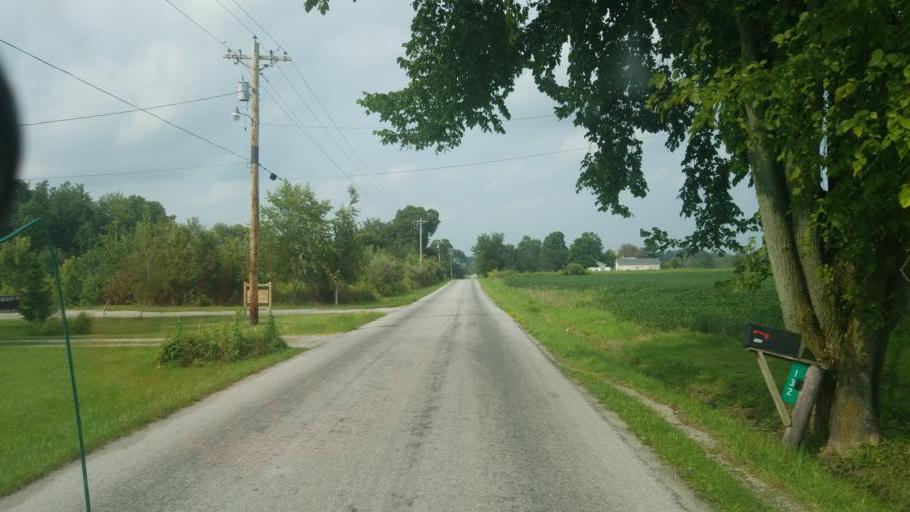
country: US
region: Ohio
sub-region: Wayne County
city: West Salem
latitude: 41.0450
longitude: -82.2017
